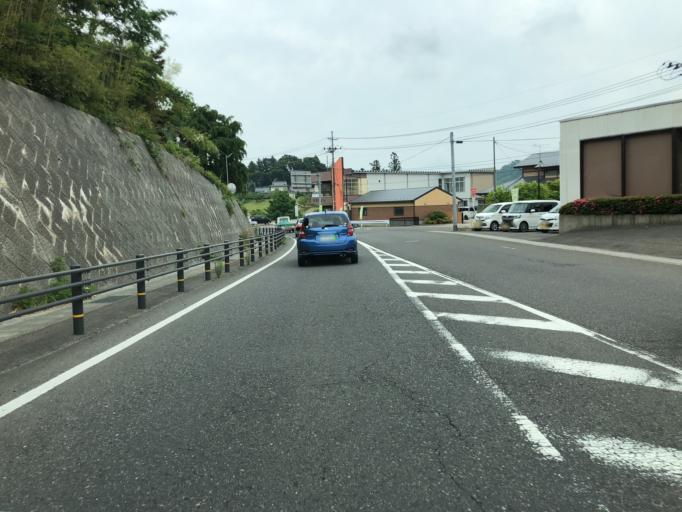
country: JP
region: Fukushima
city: Funehikimachi-funehiki
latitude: 37.4352
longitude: 140.5867
